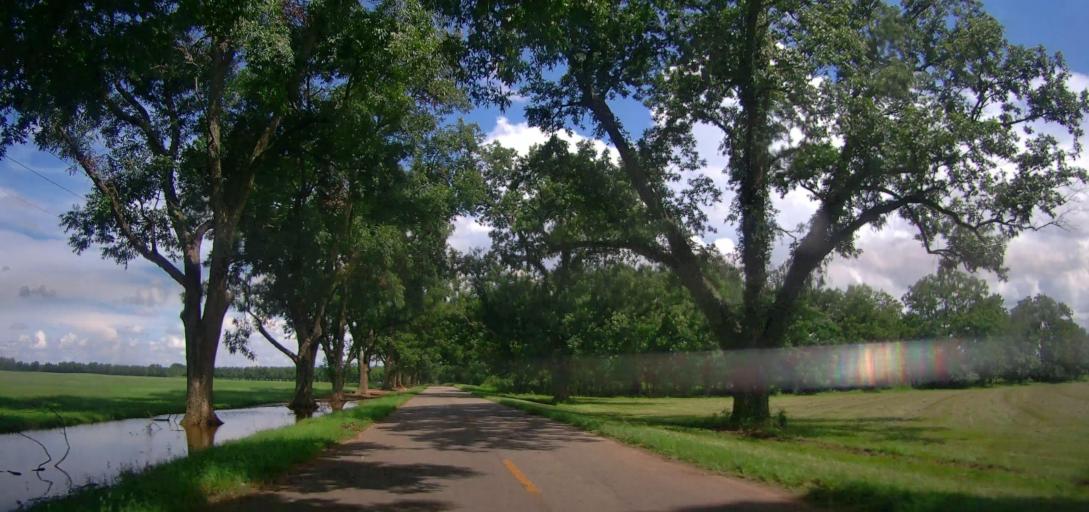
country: US
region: Georgia
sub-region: Macon County
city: Marshallville
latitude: 32.4486
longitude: -83.9899
